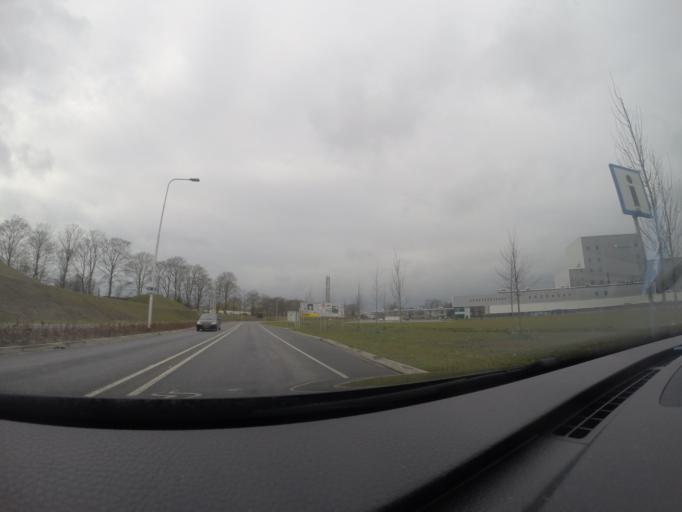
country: NL
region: Gelderland
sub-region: Berkelland
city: Borculo
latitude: 52.1162
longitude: 6.5354
